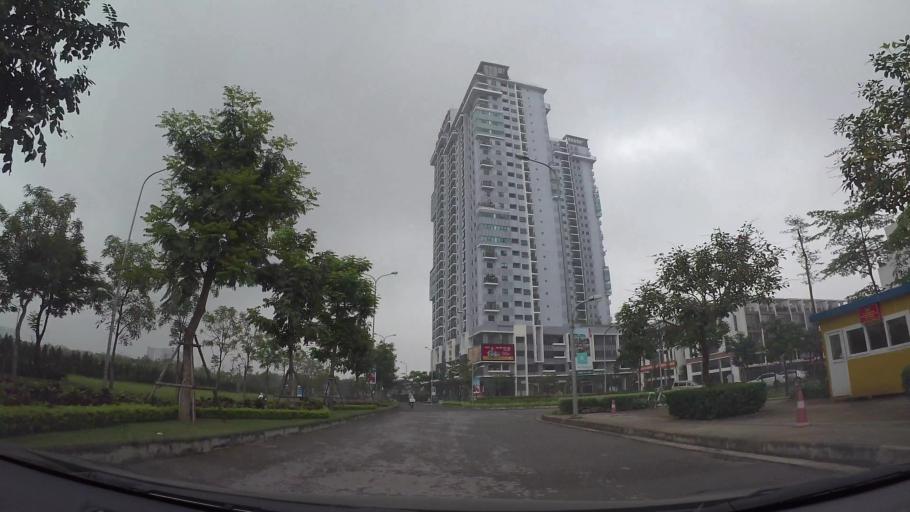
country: VN
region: Ha Noi
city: Van Dien
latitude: 20.9700
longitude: 105.8770
